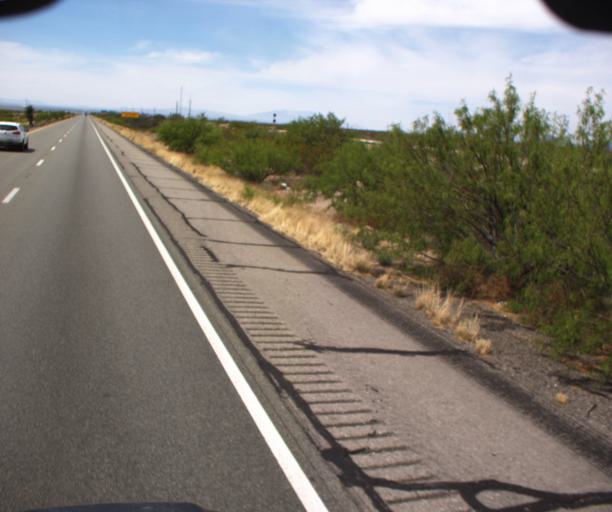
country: US
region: New Mexico
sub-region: Hidalgo County
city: Lordsburg
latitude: 32.2425
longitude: -109.1129
